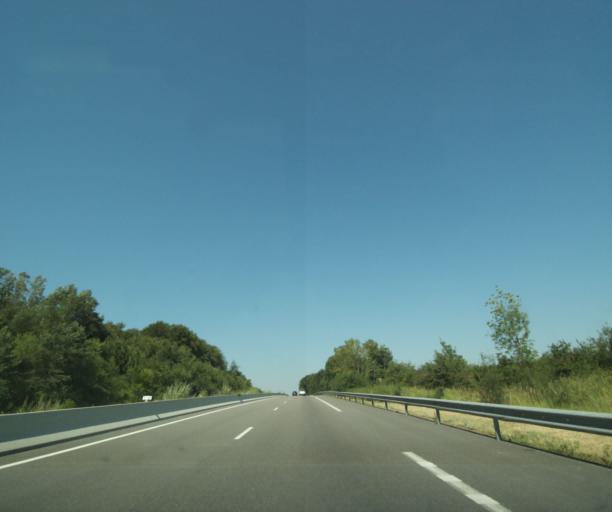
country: FR
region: Lorraine
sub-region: Departement de la Meuse
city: Lerouville
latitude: 48.7063
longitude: 5.4945
